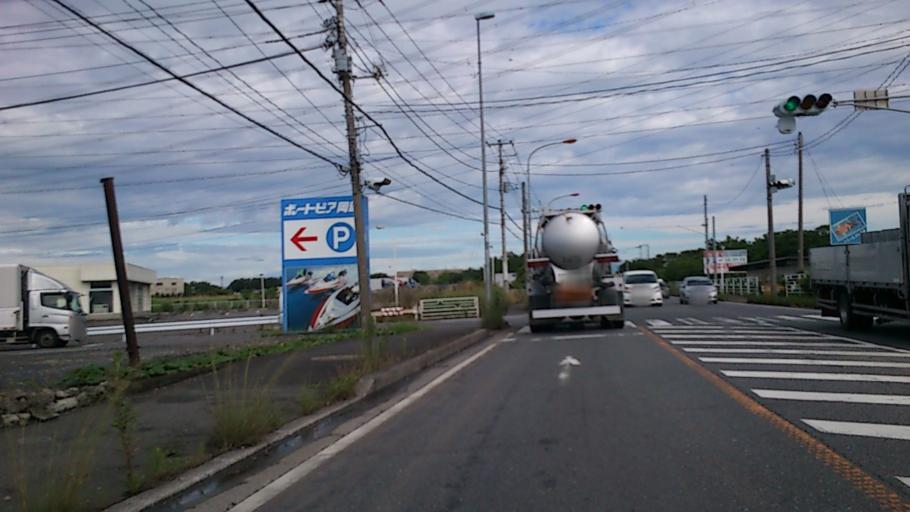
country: JP
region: Saitama
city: Honjo
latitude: 36.2253
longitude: 139.2224
